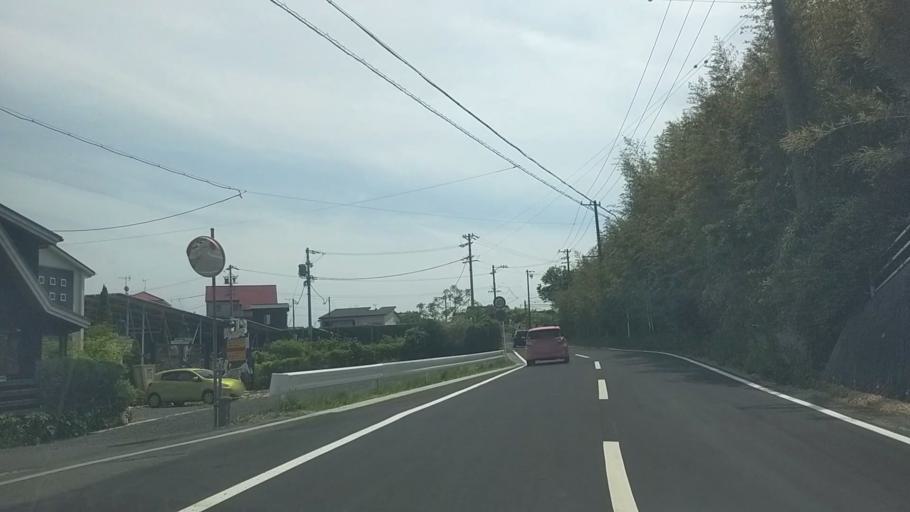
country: JP
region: Shizuoka
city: Kosai-shi
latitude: 34.7719
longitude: 137.5676
